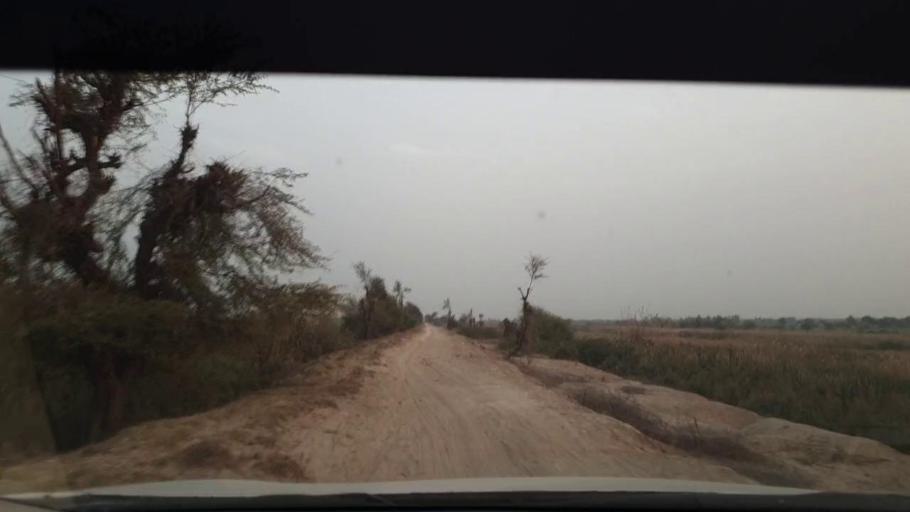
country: PK
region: Sindh
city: Berani
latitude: 25.8624
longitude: 68.7748
